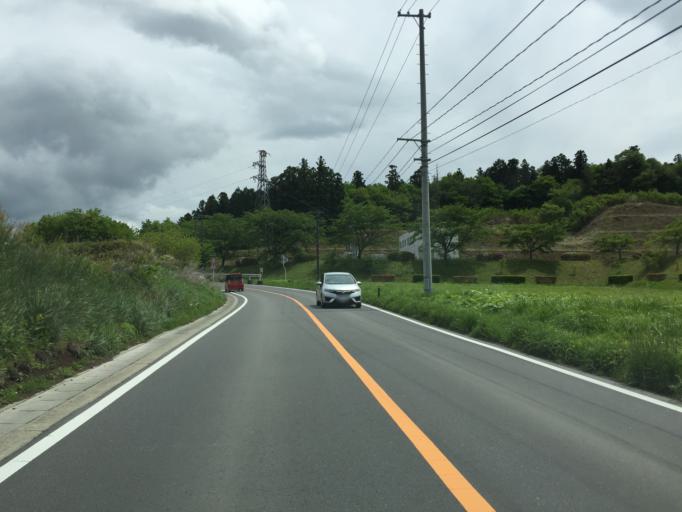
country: JP
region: Fukushima
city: Ishikawa
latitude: 37.0779
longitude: 140.3583
